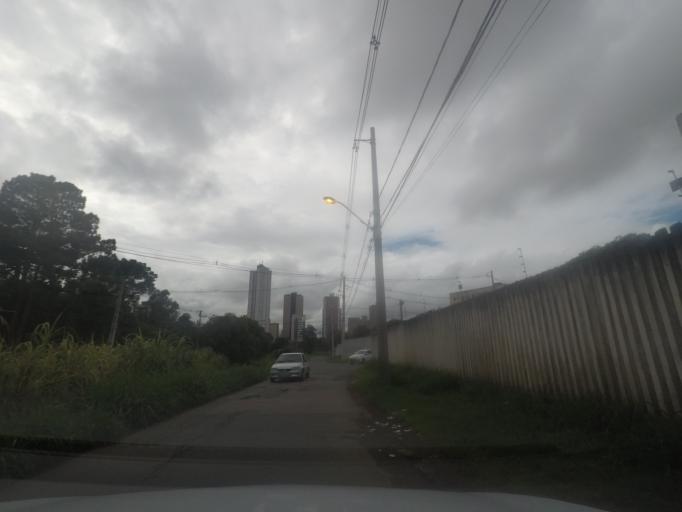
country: BR
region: Parana
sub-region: Curitiba
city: Curitiba
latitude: -25.4392
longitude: -49.2539
